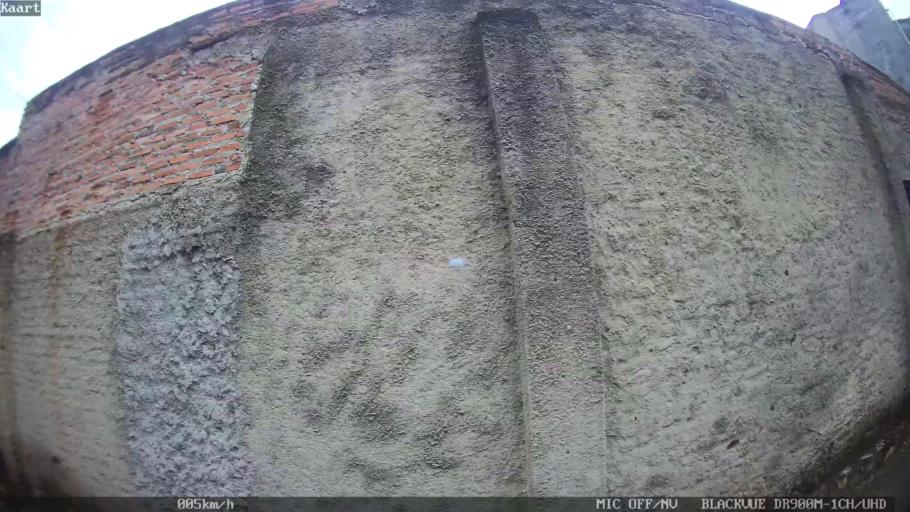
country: ID
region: Lampung
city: Kedaton
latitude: -5.3833
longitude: 105.2551
